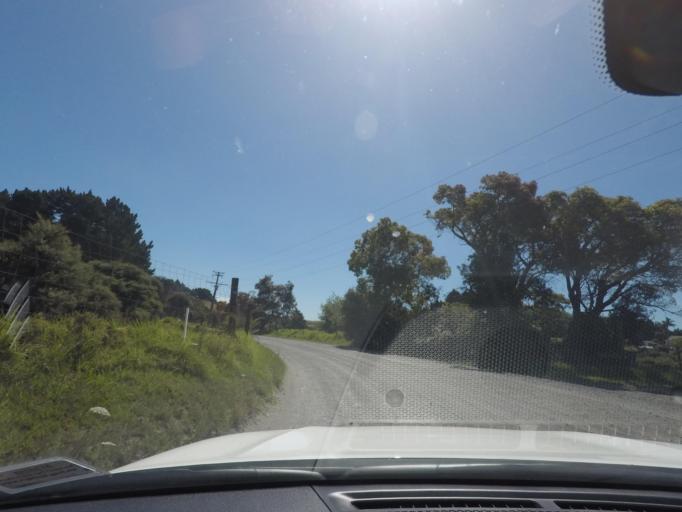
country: NZ
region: Auckland
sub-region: Auckland
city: Parakai
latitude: -36.5821
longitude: 174.3029
